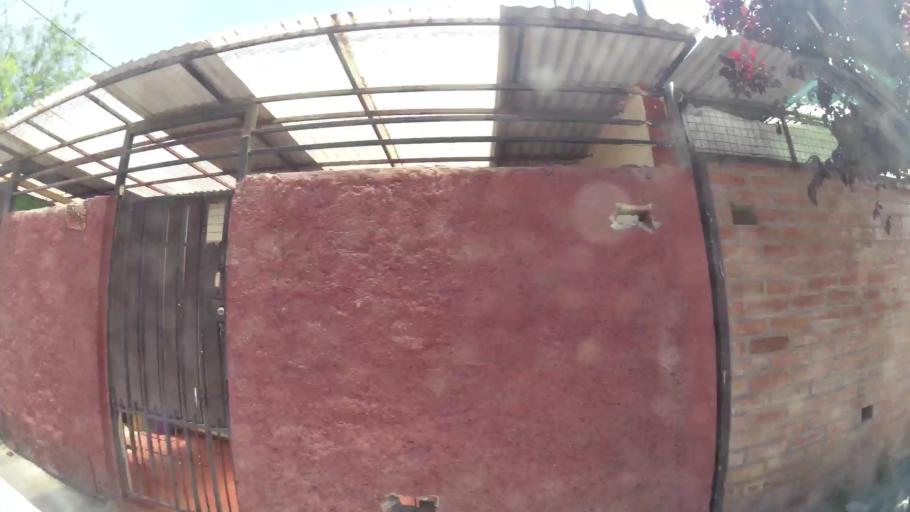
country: CL
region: Santiago Metropolitan
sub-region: Provincia de Maipo
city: San Bernardo
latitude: -33.5769
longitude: -70.6686
